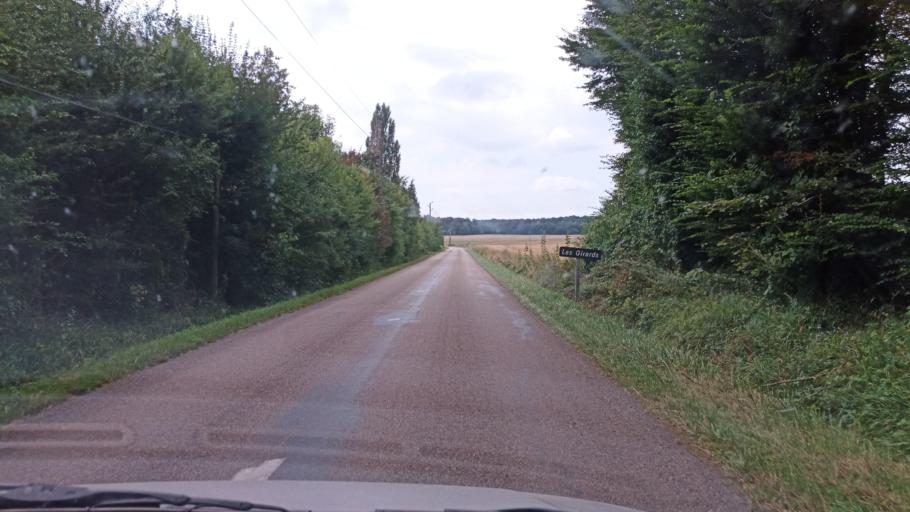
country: FR
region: Centre
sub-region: Departement du Loiret
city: Courtenay
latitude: 48.0066
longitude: 3.1524
